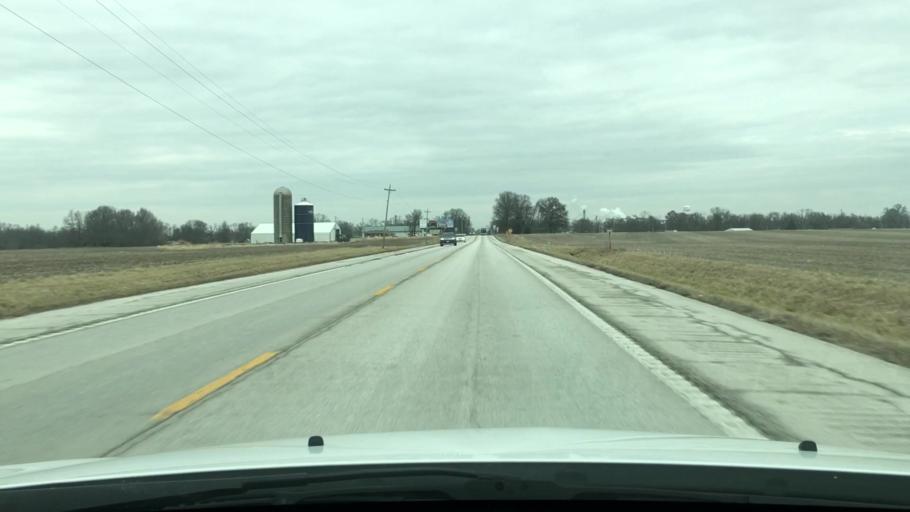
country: US
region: Missouri
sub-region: Audrain County
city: Vandalia
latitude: 39.2313
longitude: -91.6459
